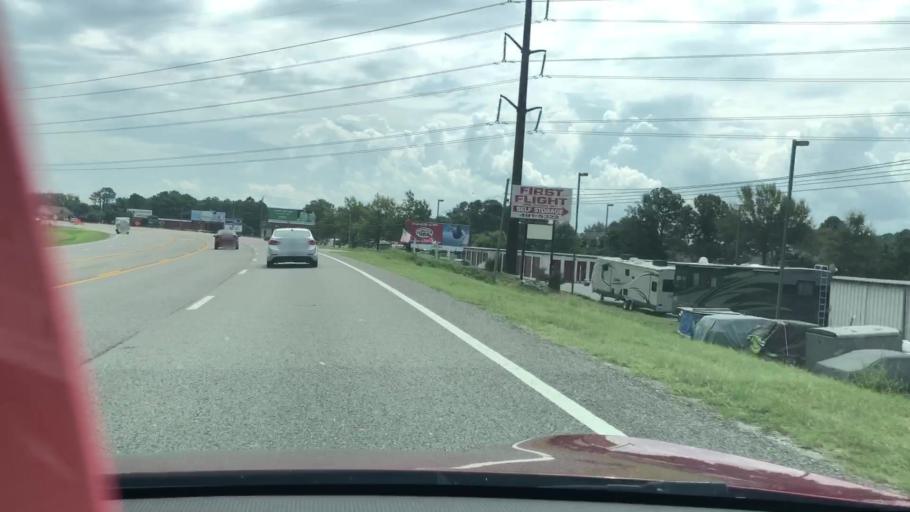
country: US
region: North Carolina
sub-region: Dare County
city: Southern Shores
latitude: 36.0833
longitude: -75.7986
